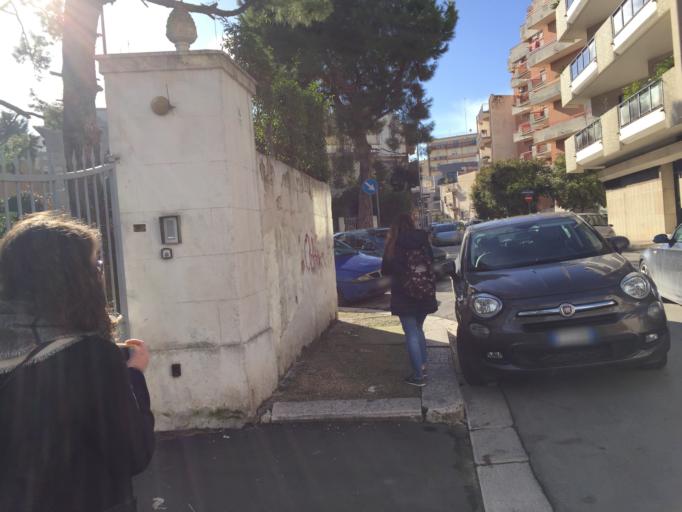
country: IT
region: Apulia
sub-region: Provincia di Barletta - Andria - Trani
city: Andria
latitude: 41.2296
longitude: 16.3052
